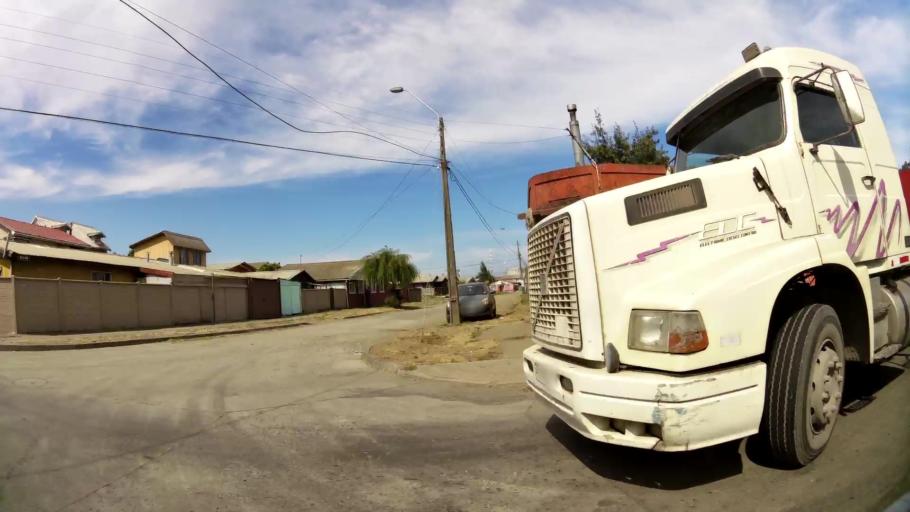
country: CL
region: Biobio
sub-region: Provincia de Concepcion
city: Talcahuano
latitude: -36.7227
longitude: -73.1247
